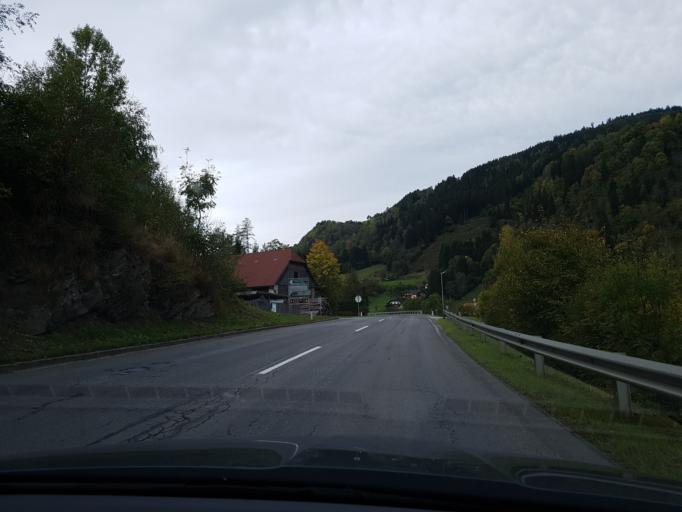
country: AT
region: Styria
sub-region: Politischer Bezirk Murau
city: Stadl an der Mur
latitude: 47.0696
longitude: 13.9114
